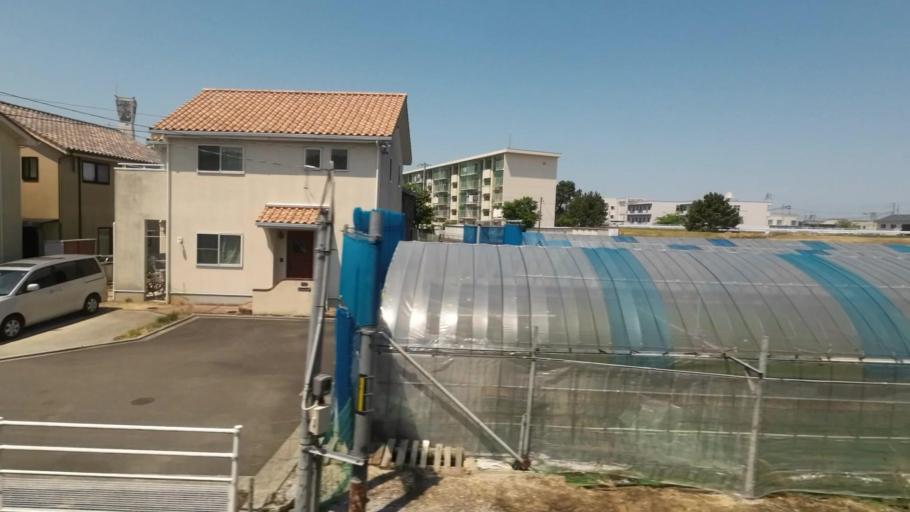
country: JP
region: Ehime
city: Hojo
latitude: 33.9458
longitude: 132.7717
